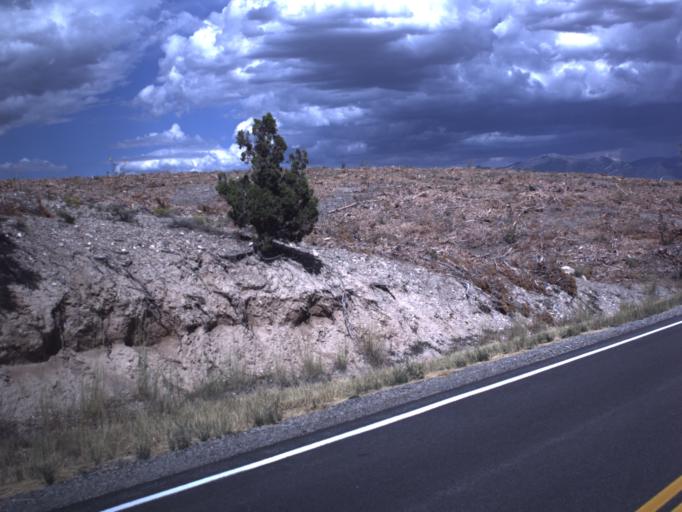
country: US
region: Utah
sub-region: Tooele County
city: Grantsville
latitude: 40.3326
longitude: -112.5186
